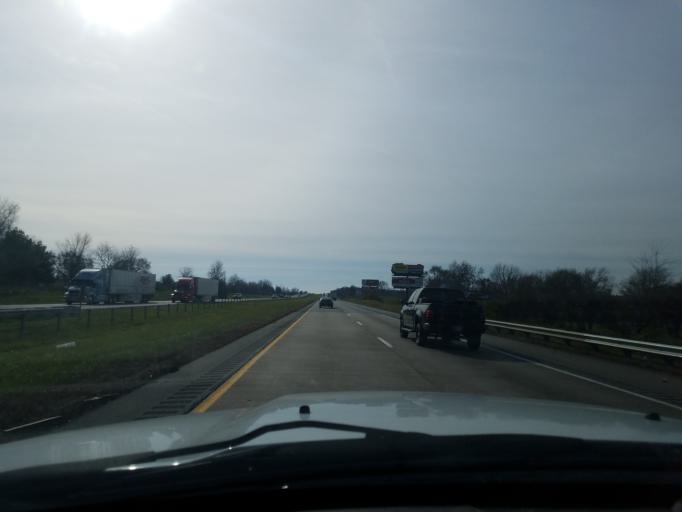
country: US
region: Indiana
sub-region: Madison County
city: Chesterfield
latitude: 40.0760
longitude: -85.5824
